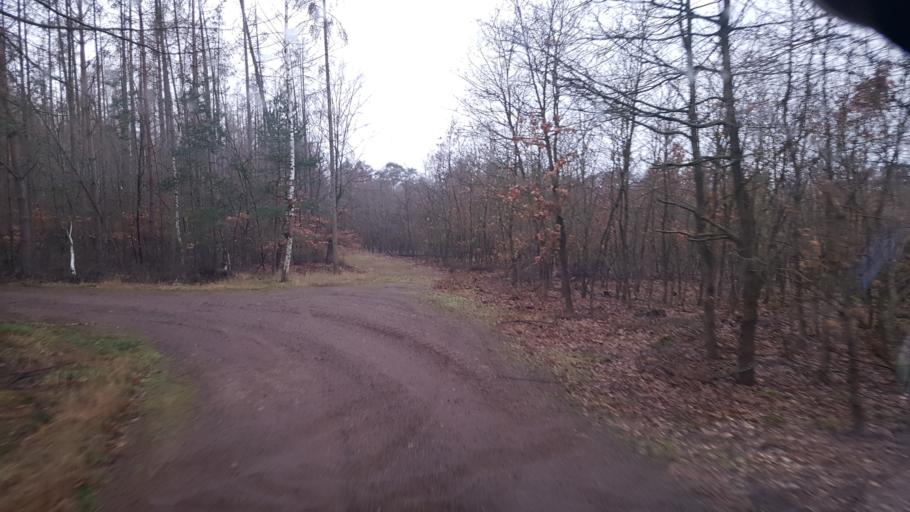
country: DE
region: Brandenburg
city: Muhlberg
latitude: 51.4915
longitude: 13.2895
